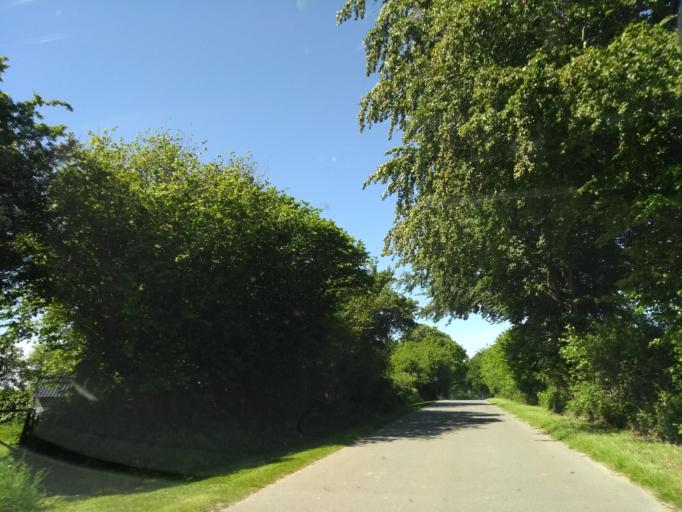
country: DE
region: Schleswig-Holstein
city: Waabs
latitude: 54.5428
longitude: 9.9572
